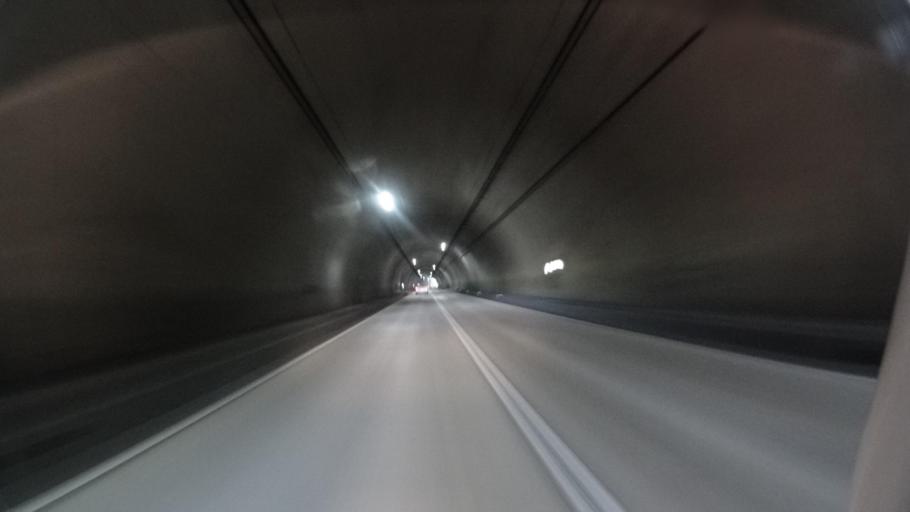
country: JP
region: Kyoto
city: Kameoka
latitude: 35.2253
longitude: 135.5728
